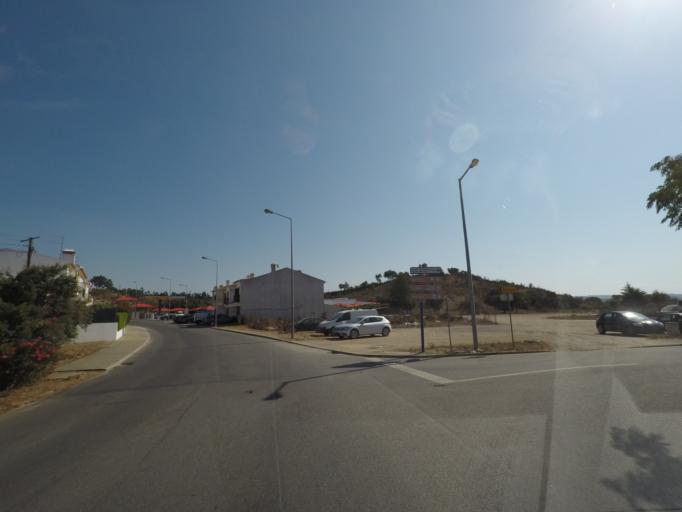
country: PT
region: Beja
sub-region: Odemira
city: Odemira
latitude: 37.5991
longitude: -8.6322
